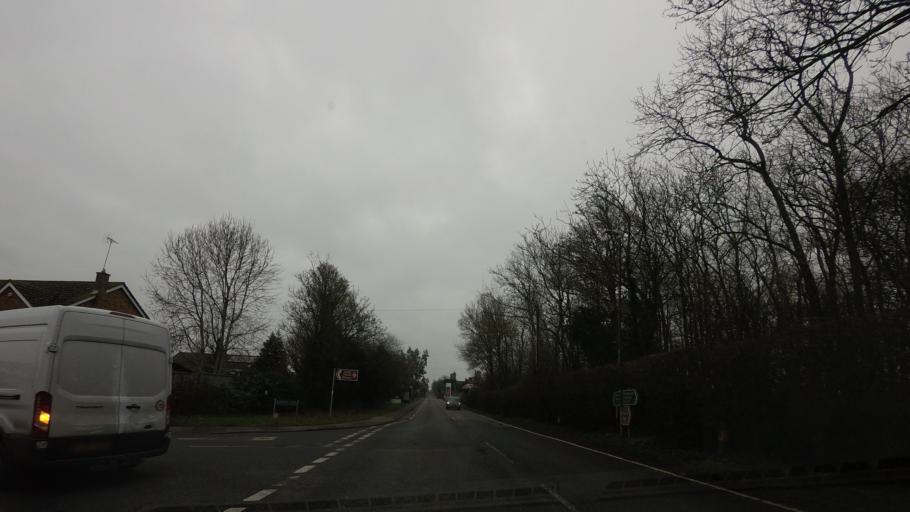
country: GB
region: England
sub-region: Kent
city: Staplehurst
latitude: 51.1539
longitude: 0.5523
